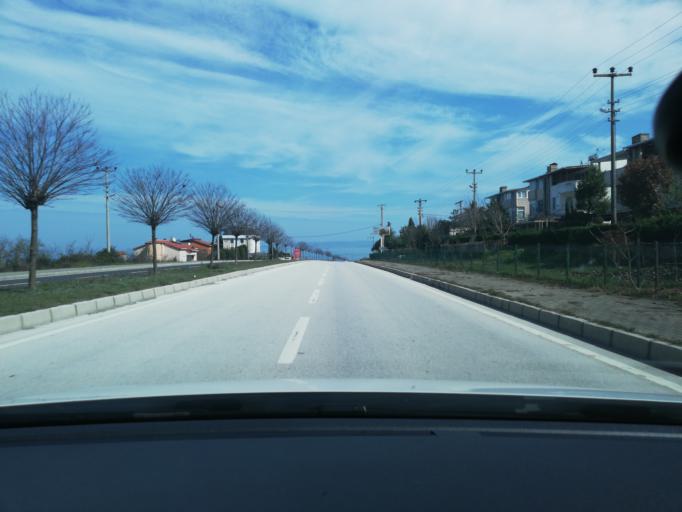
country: TR
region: Duzce
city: Akcakoca
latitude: 41.0904
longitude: 31.1858
